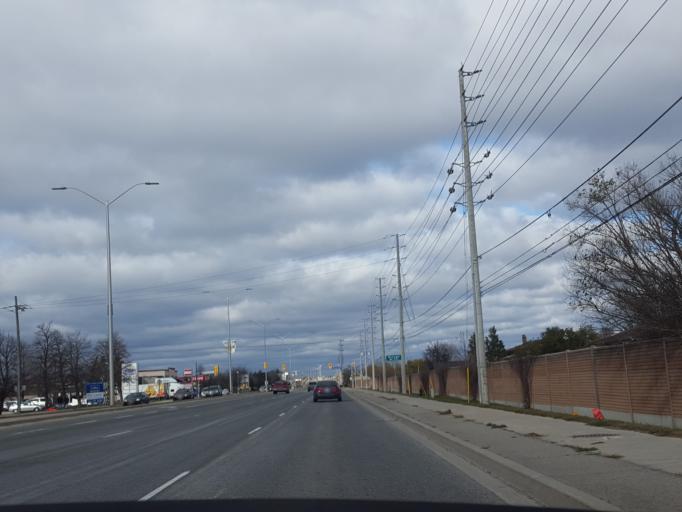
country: CA
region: Ontario
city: Etobicoke
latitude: 43.7112
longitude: -79.6523
